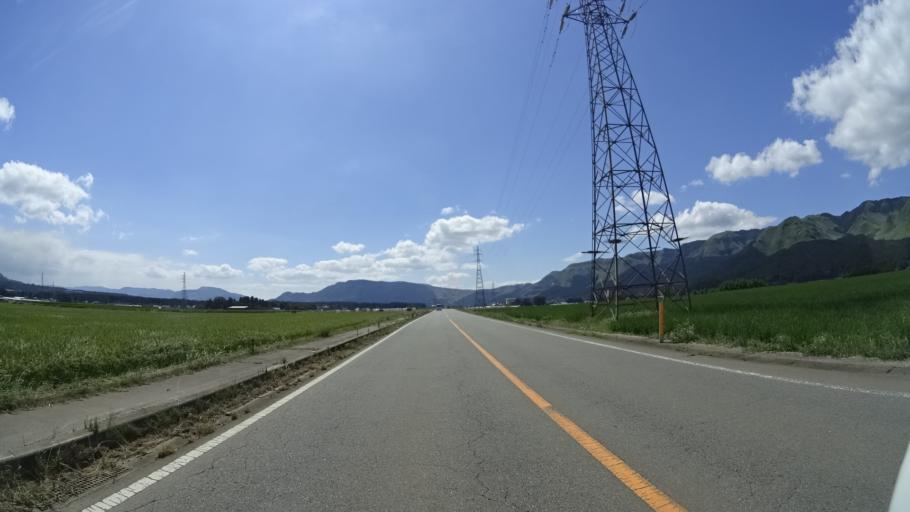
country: JP
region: Kumamoto
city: Aso
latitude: 32.9384
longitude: 131.0184
